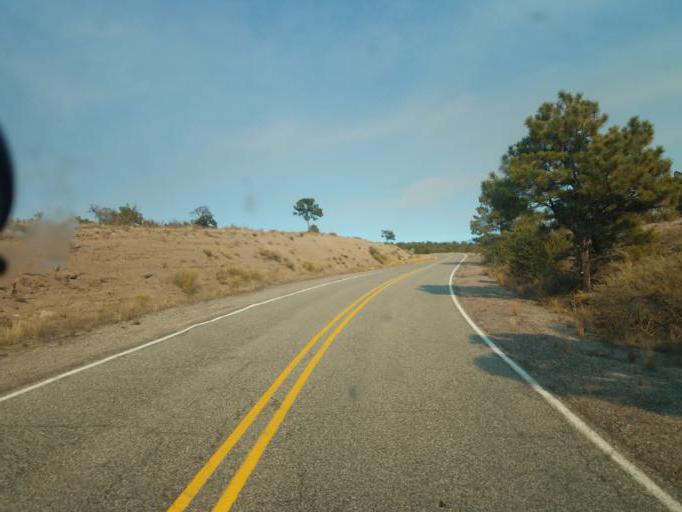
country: US
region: New Mexico
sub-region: Los Alamos County
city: White Rock
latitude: 35.7966
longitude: -106.2479
